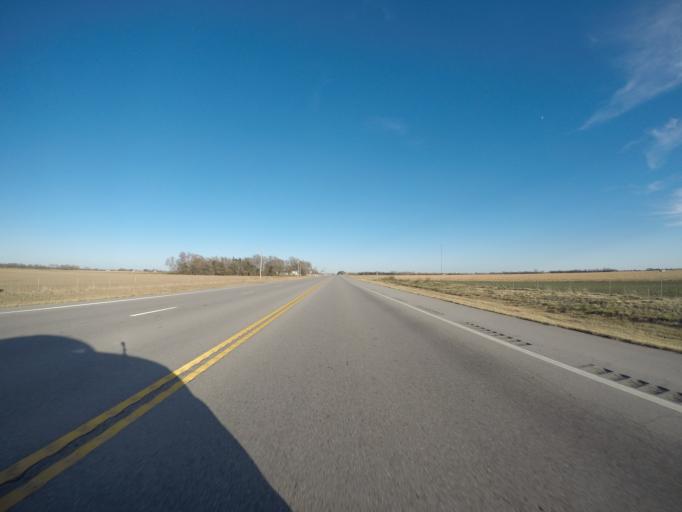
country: US
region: Kansas
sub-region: Harvey County
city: Halstead
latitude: 38.0287
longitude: -97.5721
